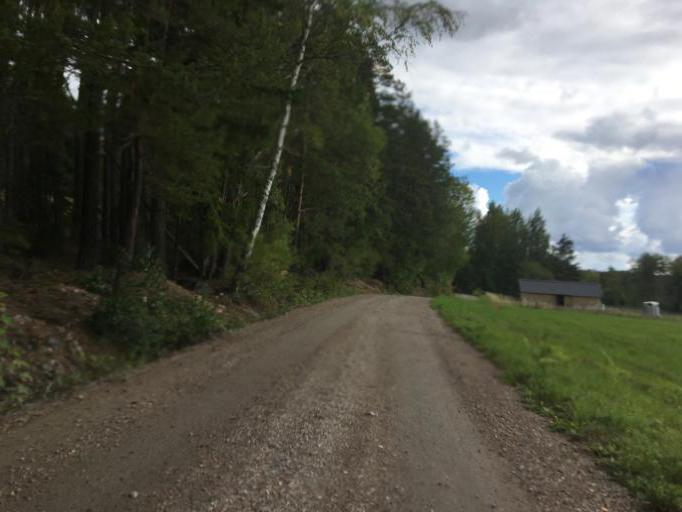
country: SE
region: Soedermanland
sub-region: Eskilstuna Kommun
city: Arla
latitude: 59.4572
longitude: 16.6795
